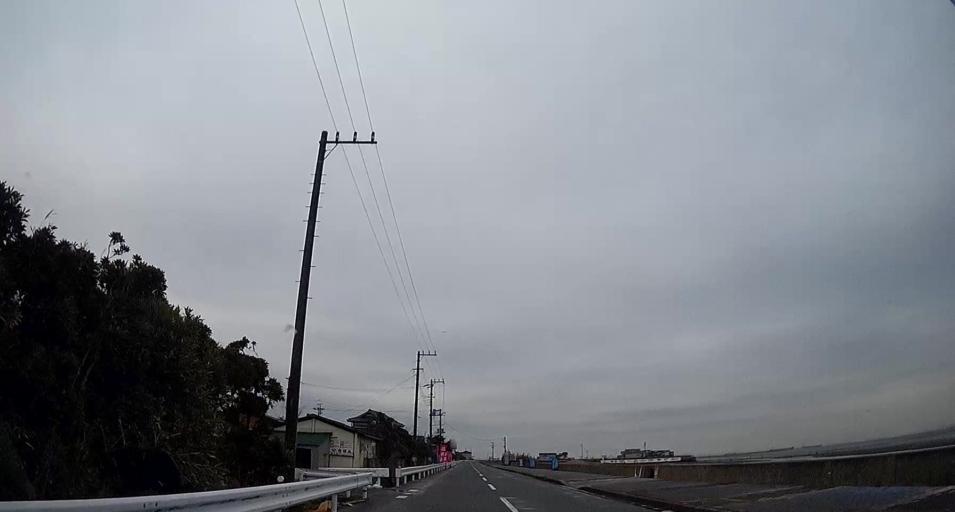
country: JP
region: Chiba
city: Kisarazu
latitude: 35.4329
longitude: 139.9091
